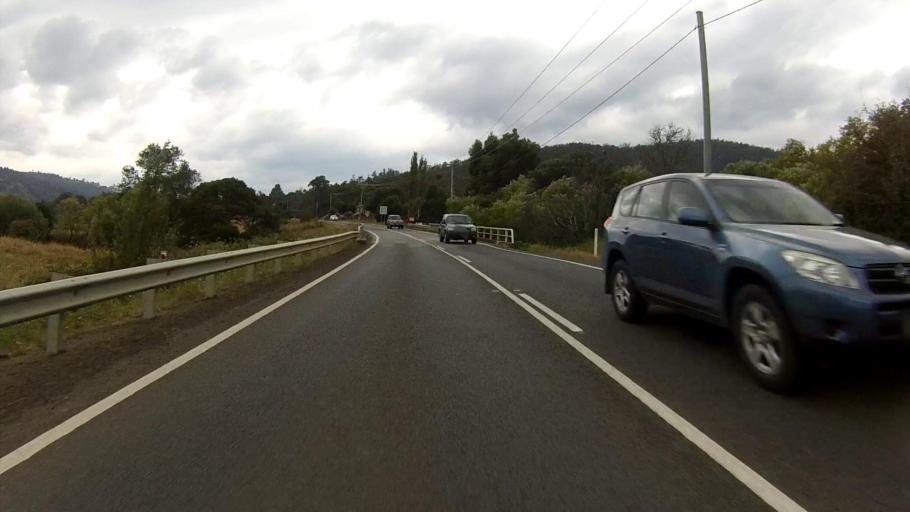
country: AU
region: Tasmania
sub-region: Huon Valley
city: Franklin
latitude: -43.0703
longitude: 147.0406
